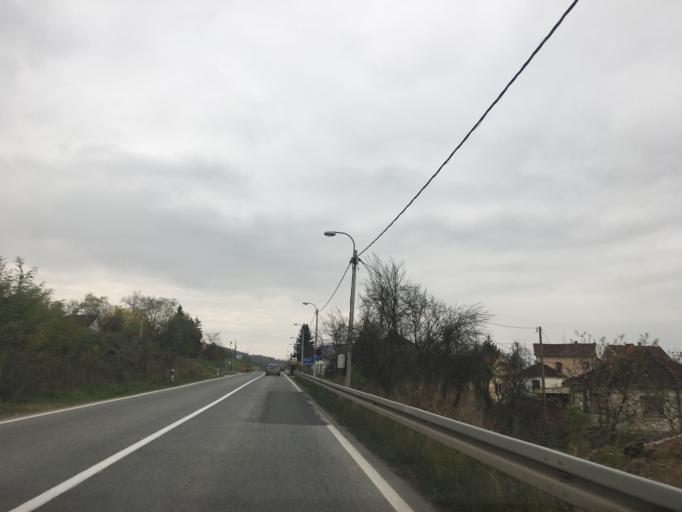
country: RS
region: Central Serbia
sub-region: Raski Okrug
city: Kraljevo
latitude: 43.7282
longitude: 20.7535
